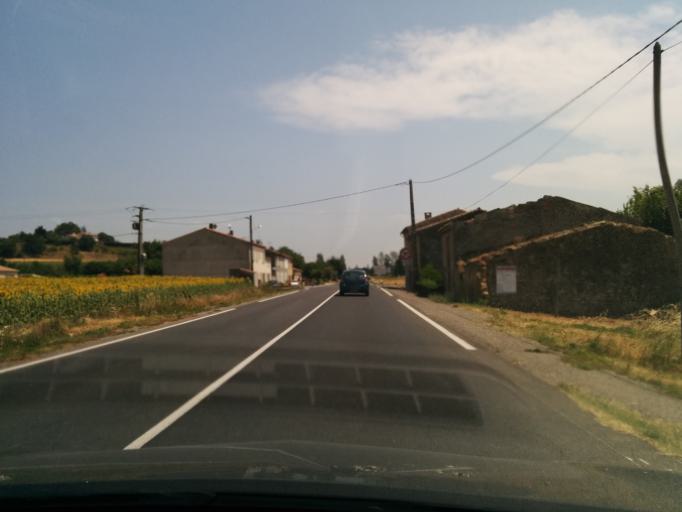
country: FR
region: Midi-Pyrenees
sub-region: Departement de la Haute-Garonne
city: Avignonet-Lauragais
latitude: 43.3567
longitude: 1.8207
